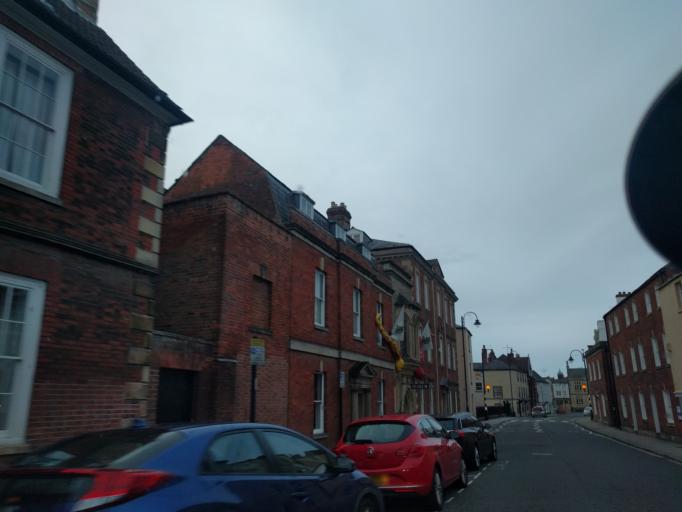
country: GB
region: England
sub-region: Wiltshire
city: Devizes
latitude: 51.3497
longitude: -1.9932
